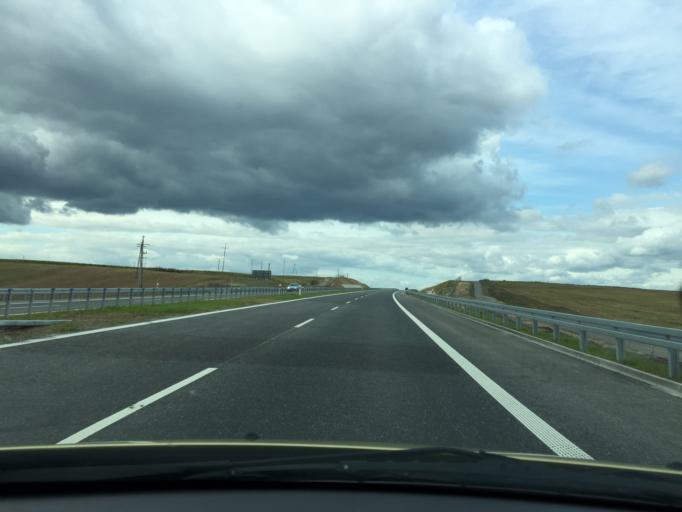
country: PL
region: Greater Poland Voivodeship
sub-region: Powiat jarocinski
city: Jarocin
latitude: 52.0026
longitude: 17.4961
